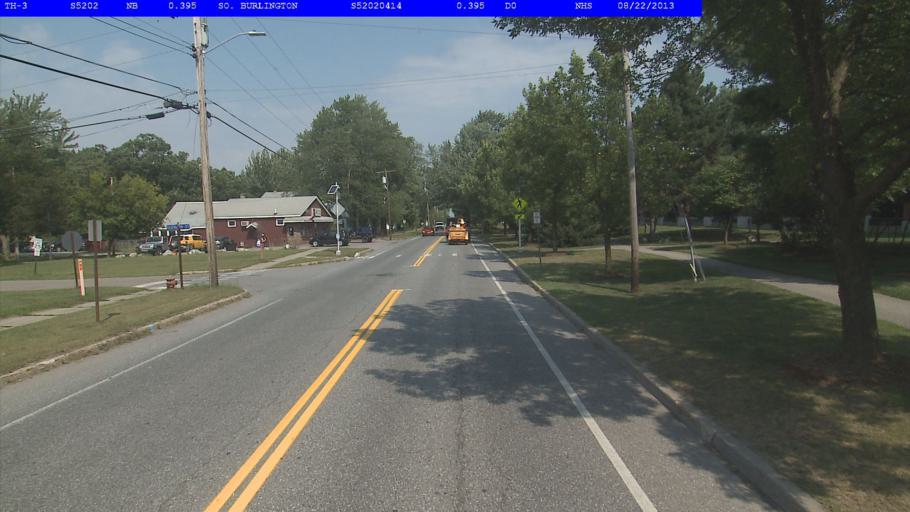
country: US
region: Vermont
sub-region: Chittenden County
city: South Burlington
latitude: 44.4685
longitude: -73.1565
